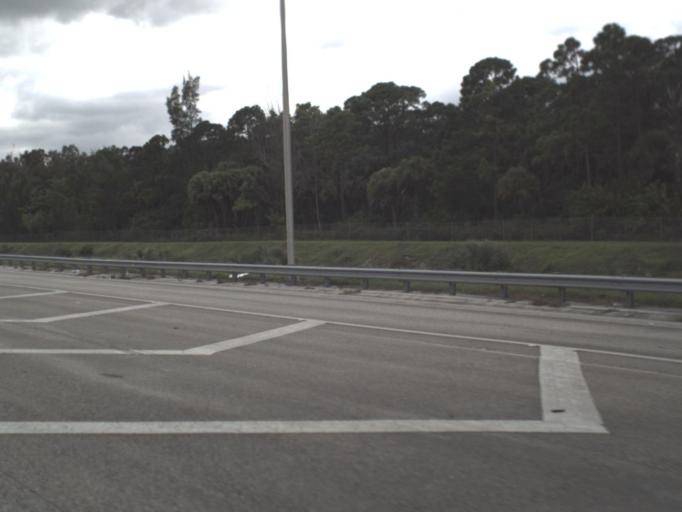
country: US
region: Florida
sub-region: Palm Beach County
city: Lake Belvedere Estates
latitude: 26.6975
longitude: -80.1511
